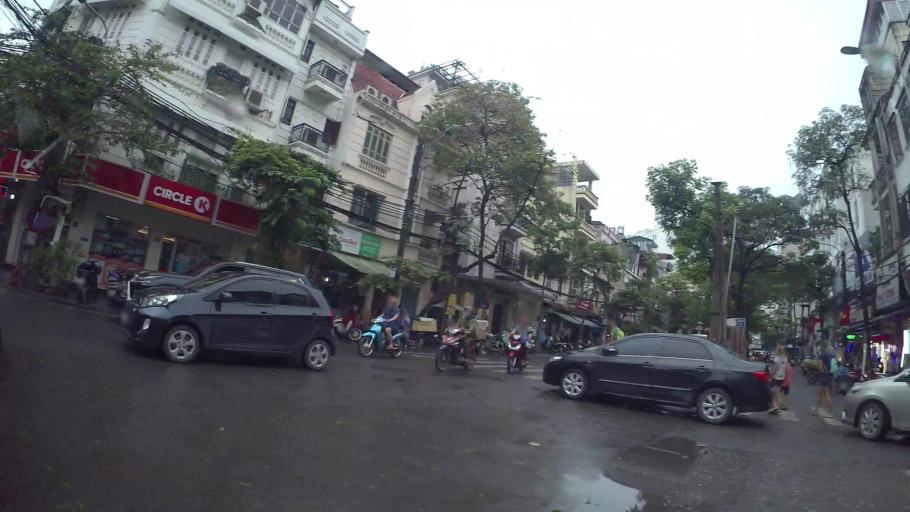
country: VN
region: Ha Noi
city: Hoan Kiem
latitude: 21.0301
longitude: 105.8446
